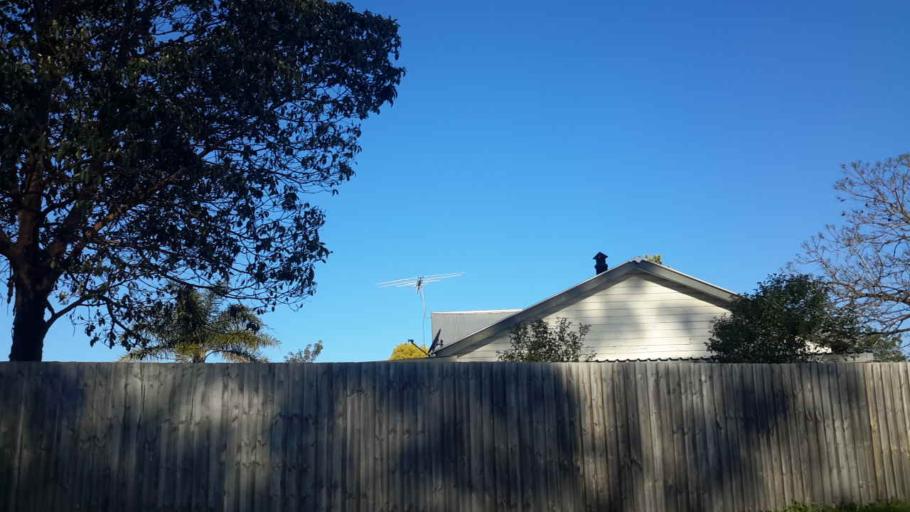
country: AU
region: New South Wales
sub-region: Penrith Municipality
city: Cambridge Park
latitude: -33.7465
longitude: 150.7147
